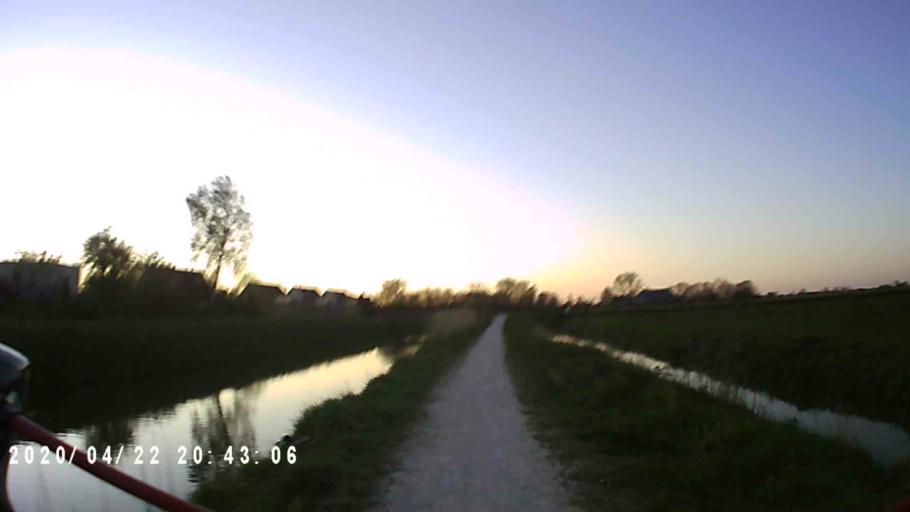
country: NL
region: Groningen
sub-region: Gemeente Winsum
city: Winsum
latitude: 53.3258
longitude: 6.5349
